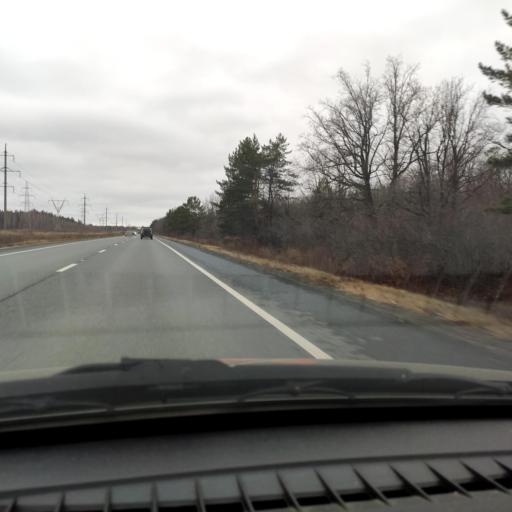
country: RU
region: Samara
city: Bogatyr'
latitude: 53.5030
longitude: 49.9464
